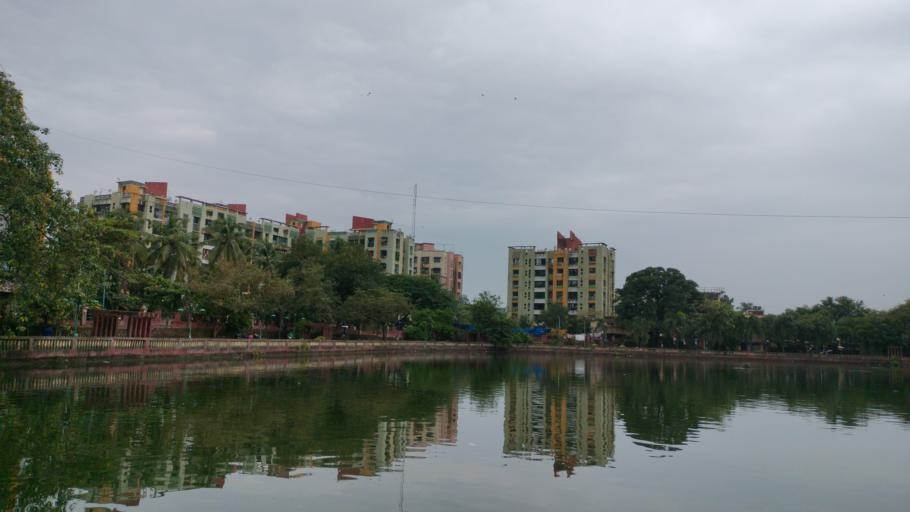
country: IN
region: Maharashtra
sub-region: Thane
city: Virar
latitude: 19.4147
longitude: 72.8619
